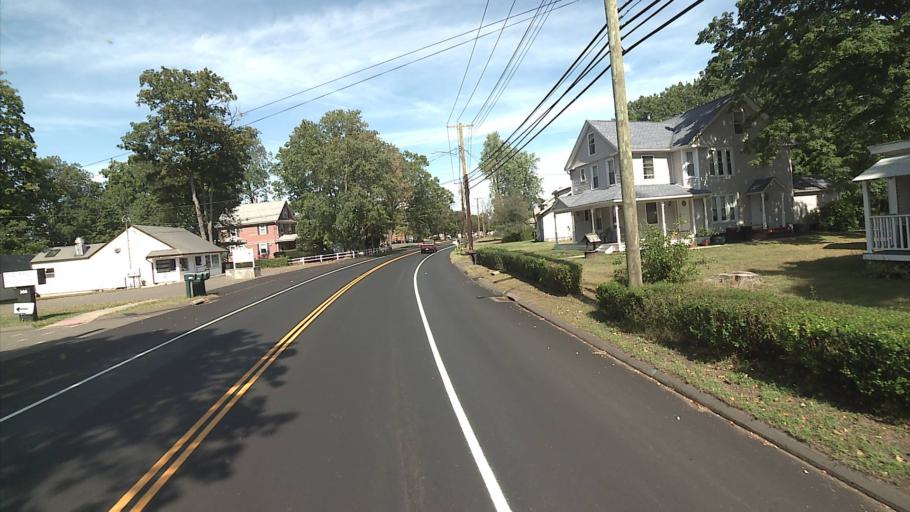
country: US
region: Connecticut
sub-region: New Haven County
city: North Haven
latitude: 41.3526
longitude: -72.8614
